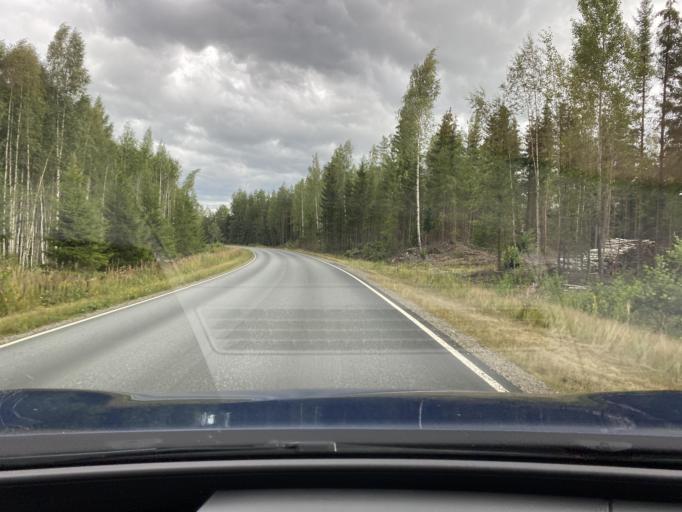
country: FI
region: Pirkanmaa
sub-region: Lounais-Pirkanmaa
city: Vammala
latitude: 61.3017
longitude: 22.9449
